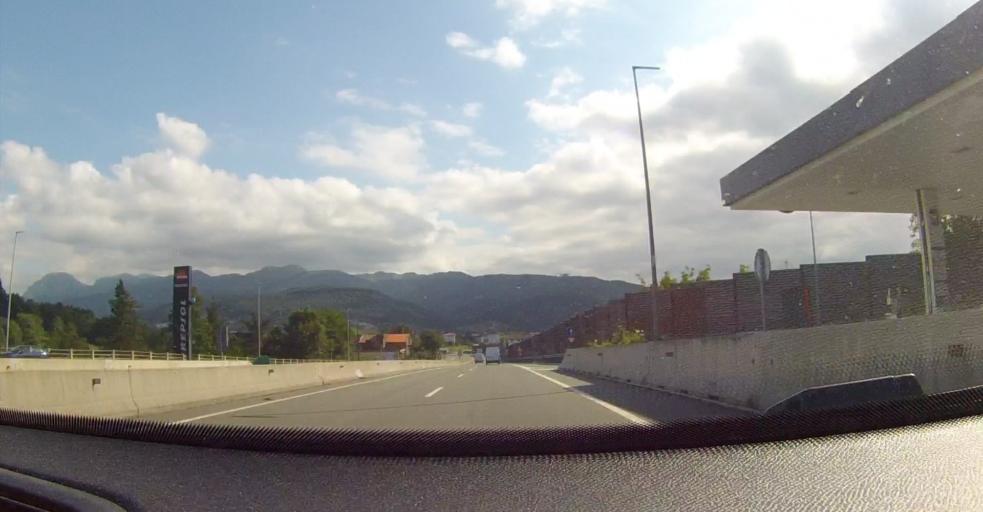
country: ES
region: Basque Country
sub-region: Bizkaia
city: Amorebieta
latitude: 43.2294
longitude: -2.7299
